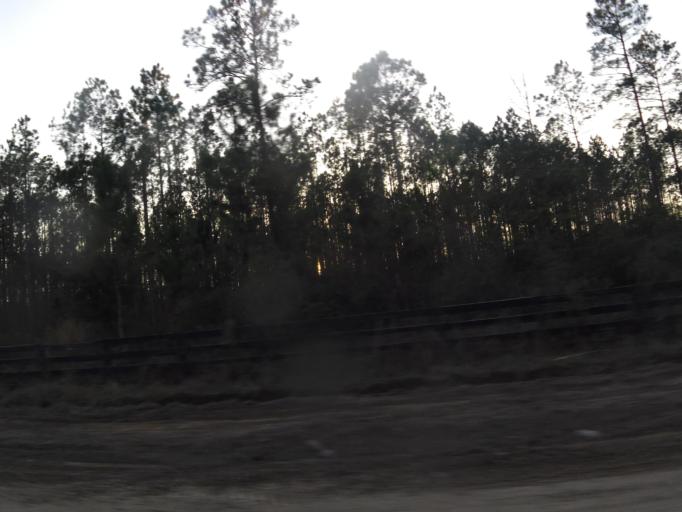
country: US
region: Florida
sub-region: Clay County
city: Green Cove Springs
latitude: 29.8638
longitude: -81.7967
